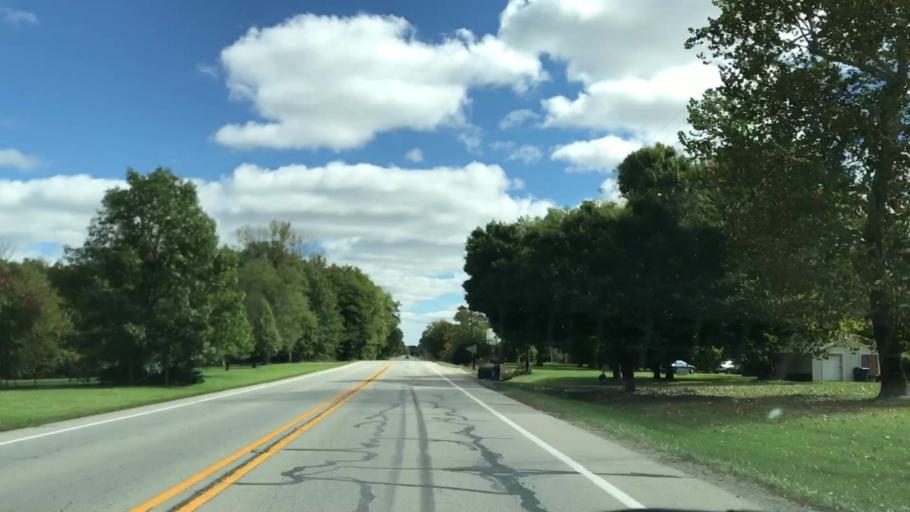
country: US
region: Indiana
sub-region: Hamilton County
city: Westfield
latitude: 40.0881
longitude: -86.1136
